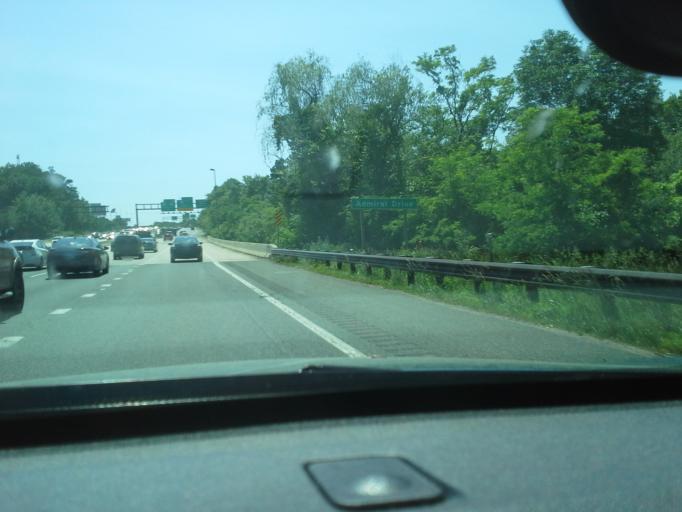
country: US
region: Maryland
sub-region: Anne Arundel County
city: Parole
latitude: 38.9909
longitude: -76.5235
